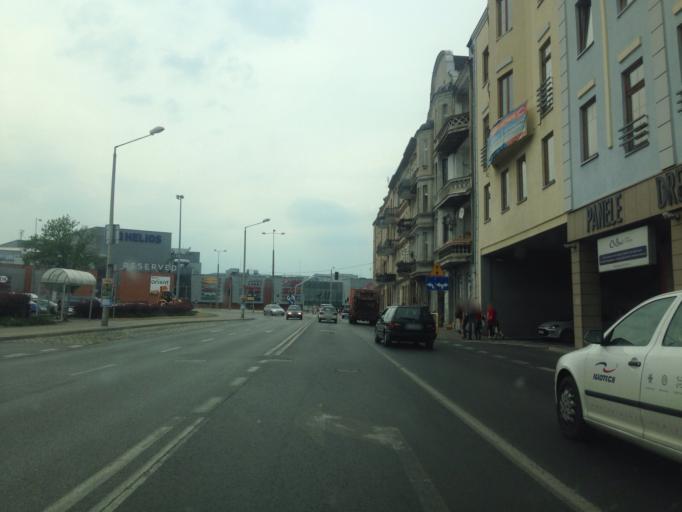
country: PL
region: Kujawsko-Pomorskie
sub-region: Grudziadz
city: Grudziadz
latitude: 53.4844
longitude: 18.7507
